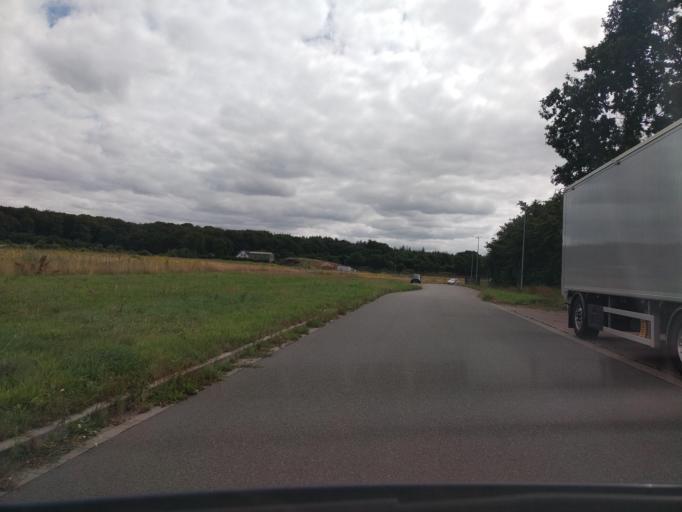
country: DE
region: Schleswig-Holstein
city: Schuby
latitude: 54.5243
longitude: 9.4962
